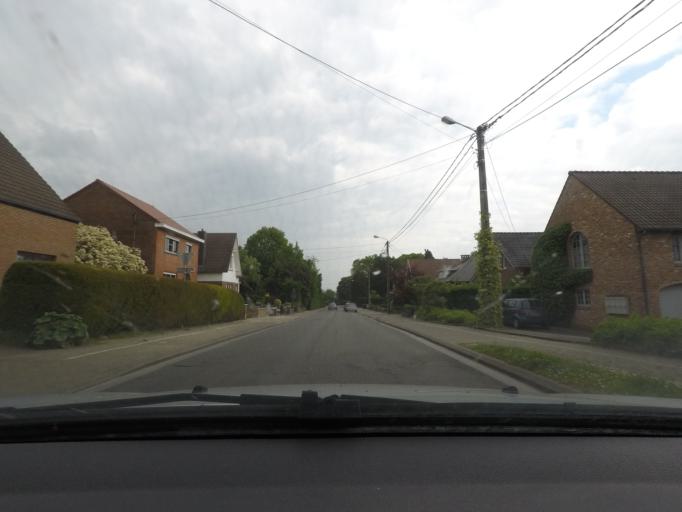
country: BE
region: Wallonia
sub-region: Province du Brabant Wallon
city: Ottignies
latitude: 50.6626
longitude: 4.5543
